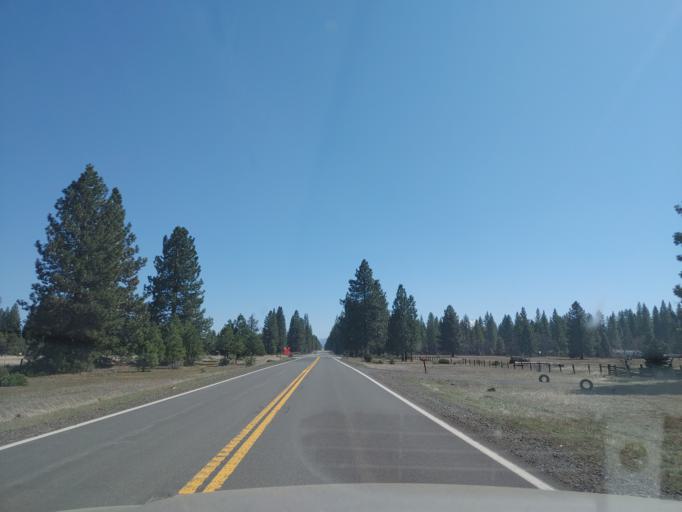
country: US
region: California
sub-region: Shasta County
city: Burney
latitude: 41.0035
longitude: -121.6321
